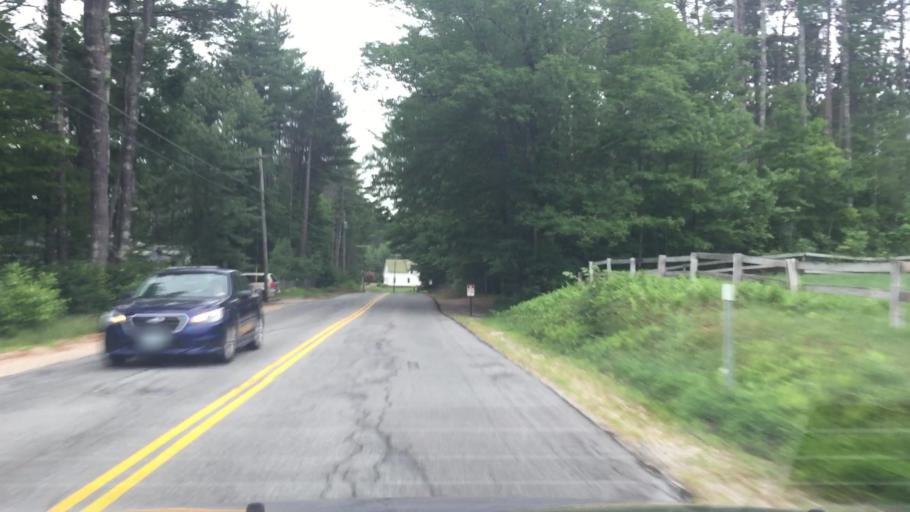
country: US
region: New Hampshire
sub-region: Carroll County
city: North Conway
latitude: 44.0702
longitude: -71.1605
